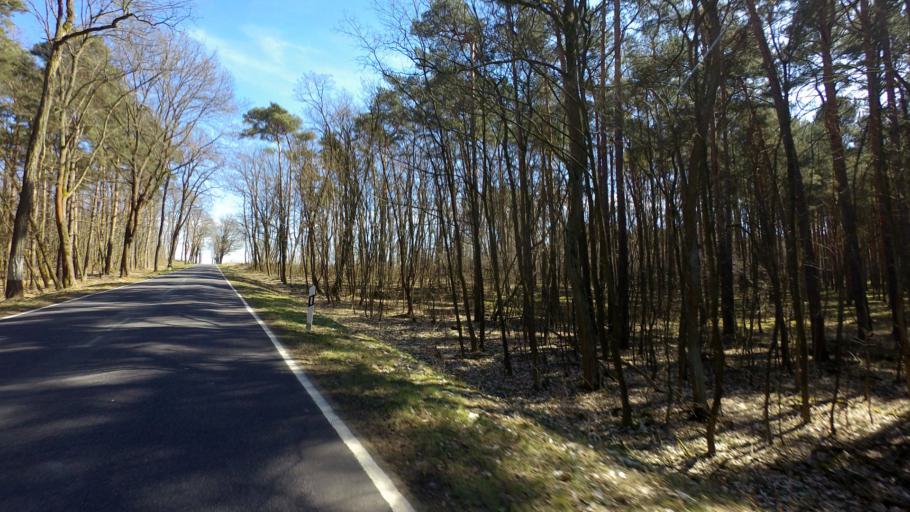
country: DE
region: Brandenburg
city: Munchehofe
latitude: 52.1600
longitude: 13.9012
